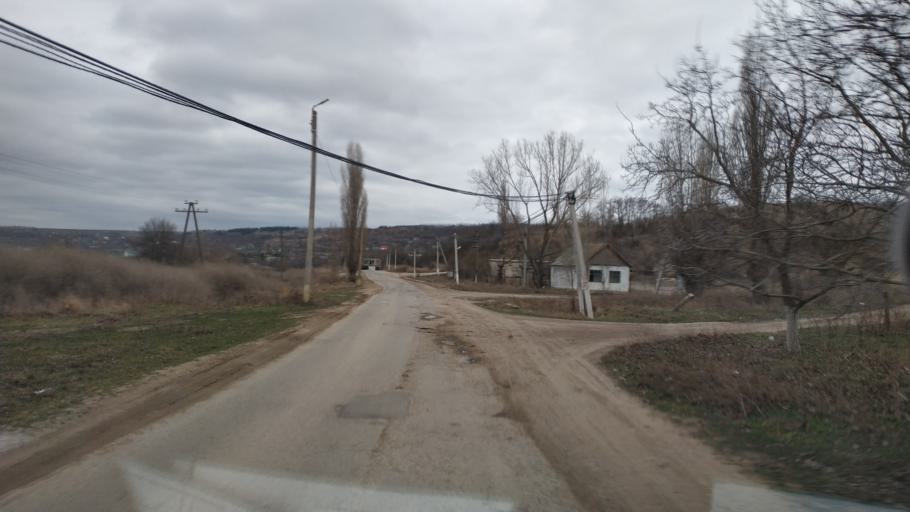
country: MD
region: Bender
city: Bender
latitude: 46.7697
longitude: 29.4815
